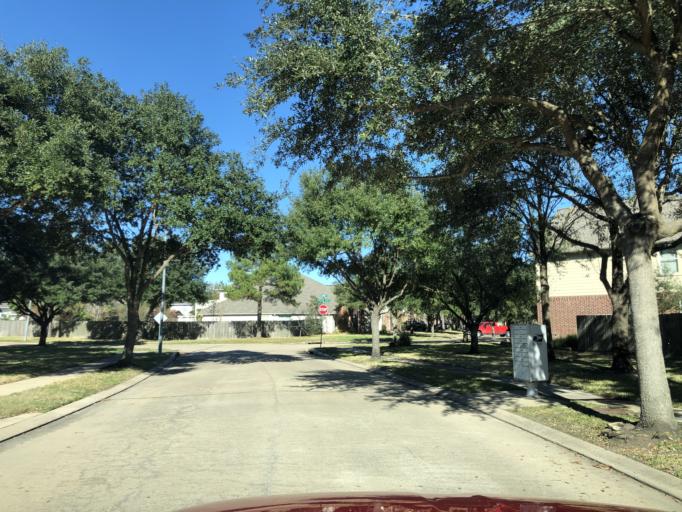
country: US
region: Texas
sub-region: Harris County
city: Oak Cliff Place
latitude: 29.9339
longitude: -95.6602
